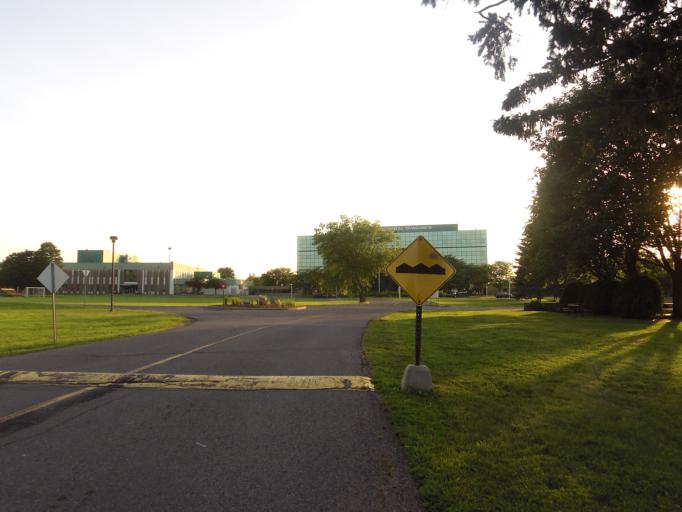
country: CA
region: Ontario
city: Bells Corners
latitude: 45.3285
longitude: -75.8237
